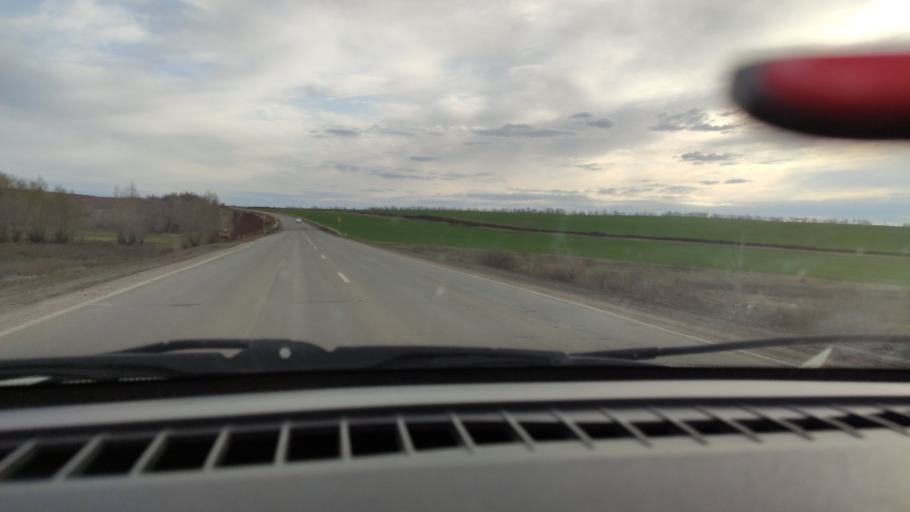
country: RU
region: Orenburg
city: Sakmara
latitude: 52.1883
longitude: 55.2978
